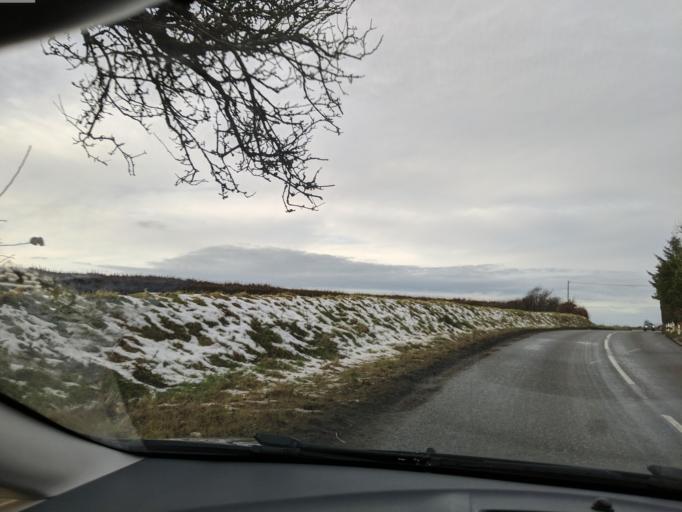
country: GB
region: England
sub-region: Cornwall
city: Jacobstow
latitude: 50.6653
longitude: -4.5930
